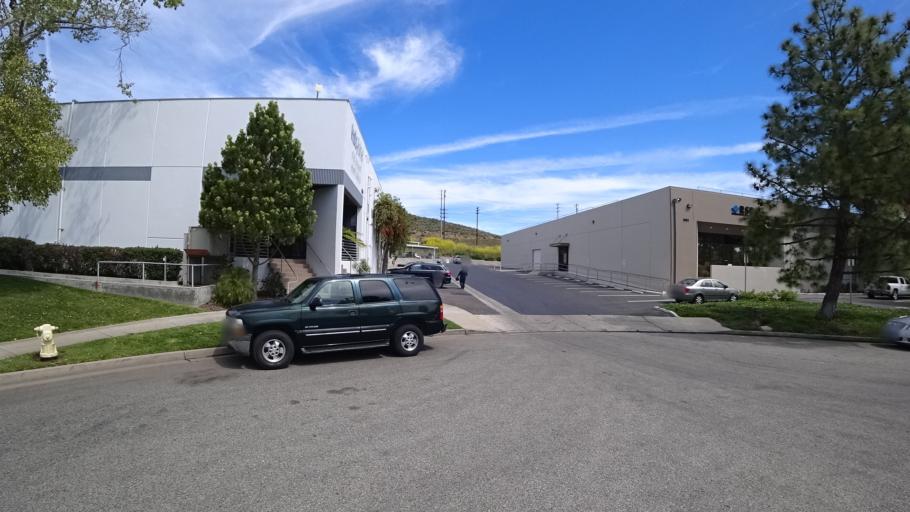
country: US
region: California
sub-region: Ventura County
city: Casa Conejo
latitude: 34.1946
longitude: -118.9326
